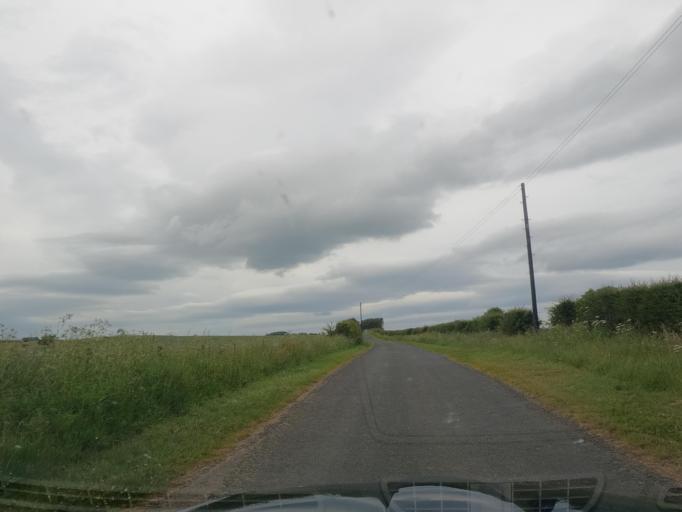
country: GB
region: England
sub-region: Northumberland
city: Lowick
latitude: 55.6203
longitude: -1.9712
